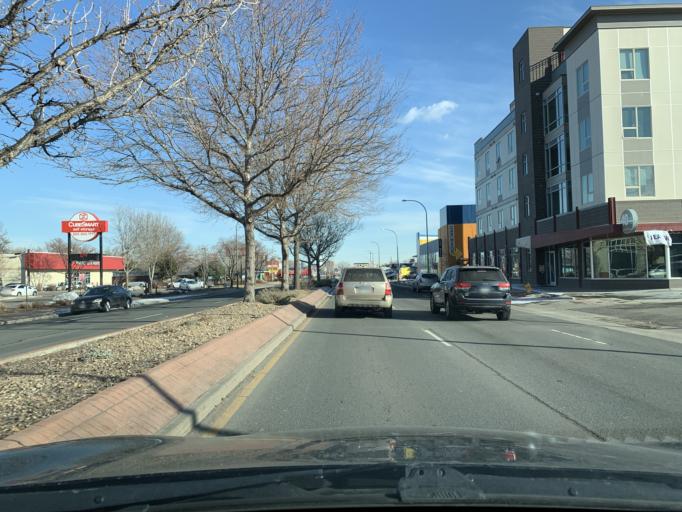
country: US
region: Colorado
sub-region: Jefferson County
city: Edgewater
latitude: 39.7403
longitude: -105.0617
